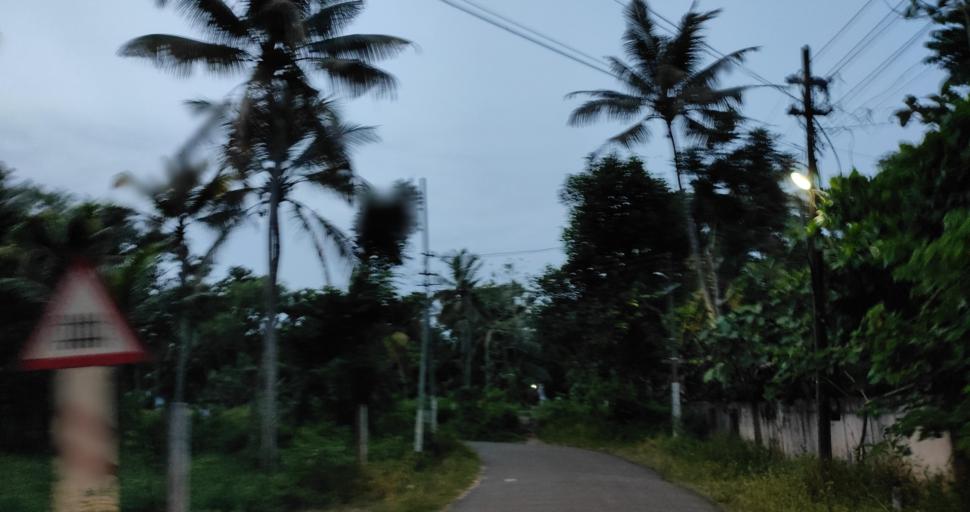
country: IN
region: Kerala
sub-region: Alappuzha
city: Vayalar
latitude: 9.7021
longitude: 76.3132
